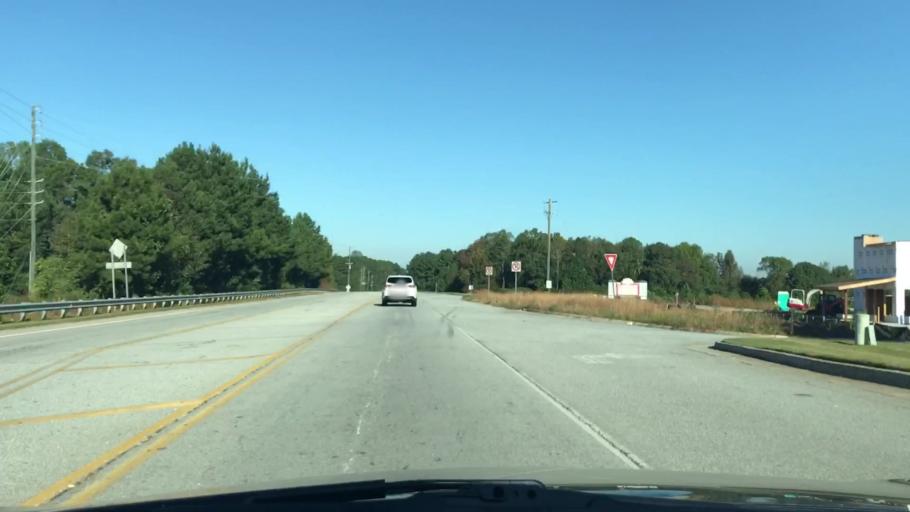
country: US
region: Georgia
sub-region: Carroll County
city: Villa Rica
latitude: 33.7331
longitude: -84.9010
